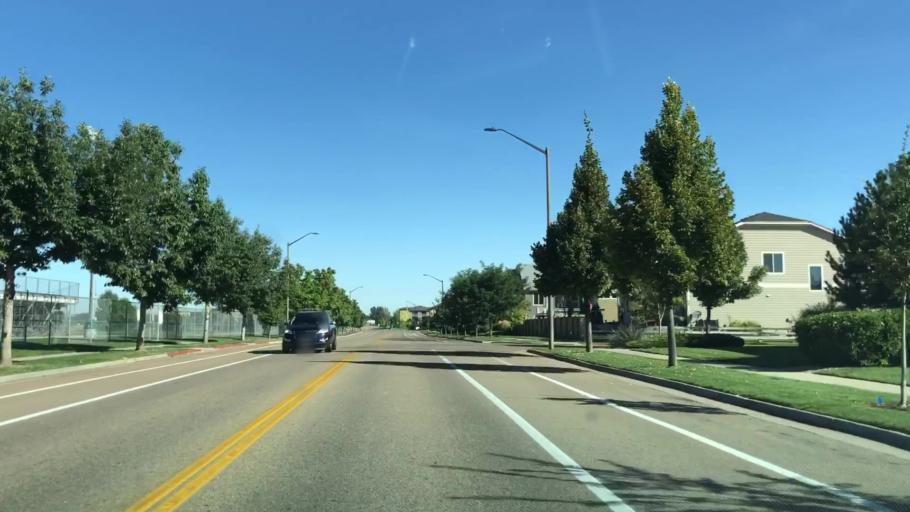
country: US
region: Colorado
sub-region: Larimer County
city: Fort Collins
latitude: 40.5140
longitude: -105.0105
